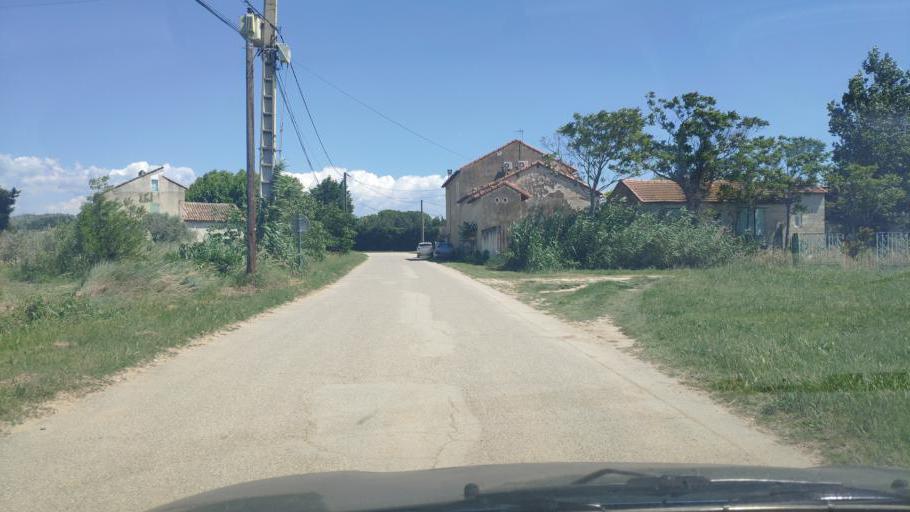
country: FR
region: Provence-Alpes-Cote d'Azur
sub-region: Departement du Vaucluse
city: Aubignan
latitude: 44.0789
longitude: 5.0203
